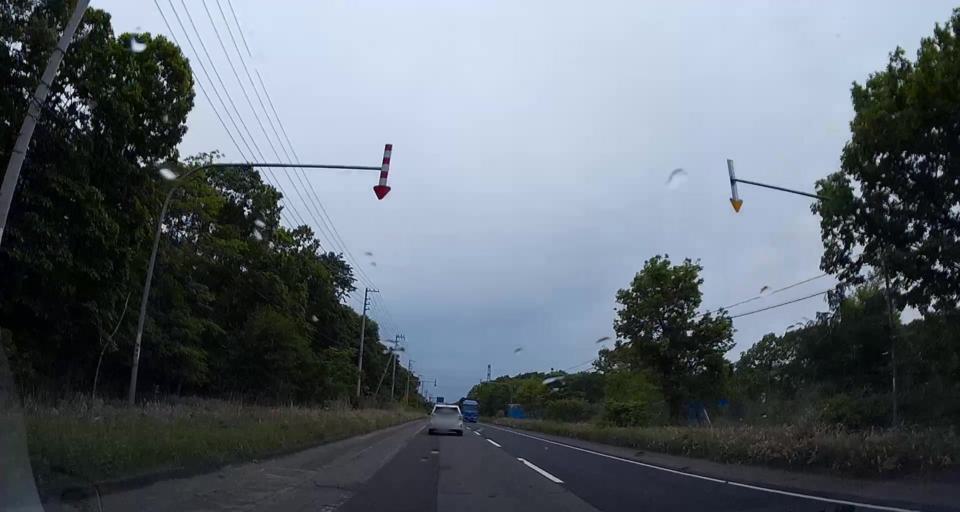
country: JP
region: Hokkaido
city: Chitose
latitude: 42.7130
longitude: 141.7510
